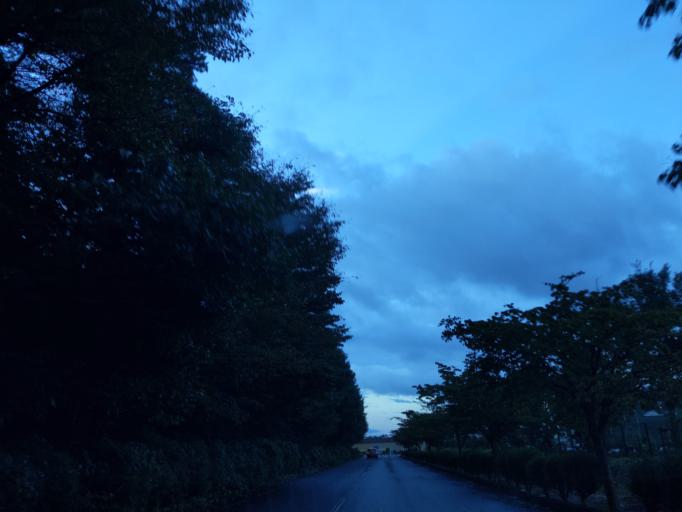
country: JP
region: Tochigi
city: Kuroiso
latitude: 36.9684
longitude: 139.9887
